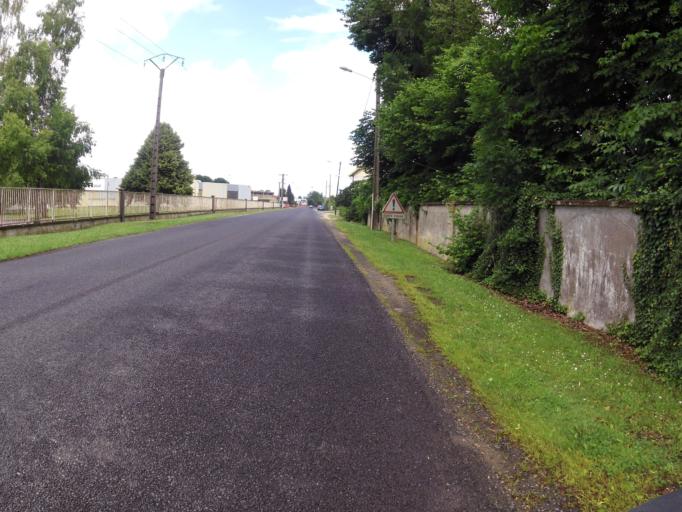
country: FR
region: Lorraine
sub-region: Departement de la Meuse
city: Revigny-sur-Ornain
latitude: 48.8175
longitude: 4.9781
